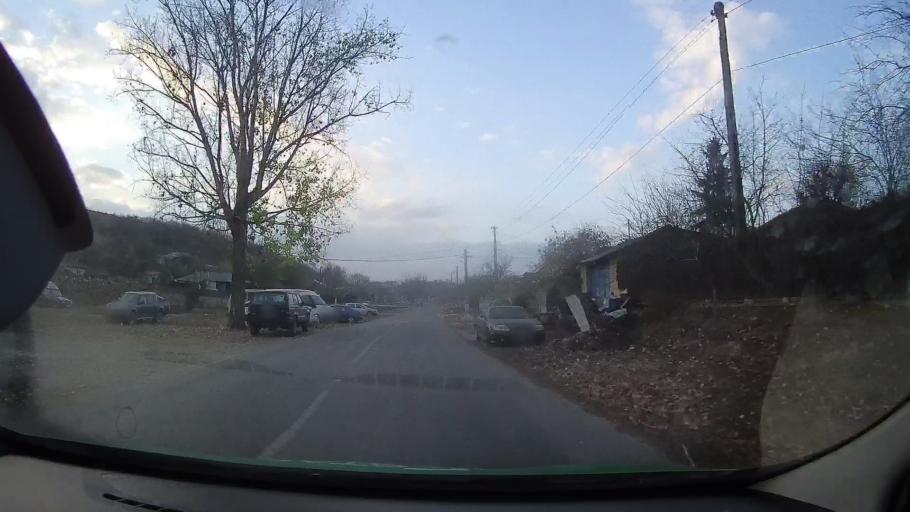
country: RO
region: Constanta
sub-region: Comuna Baneasa
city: Baneasa
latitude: 44.0606
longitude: 27.7075
